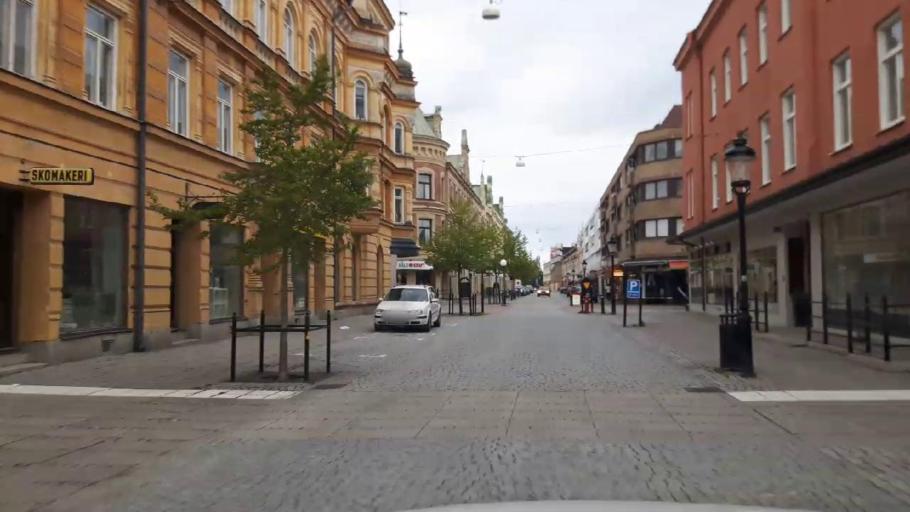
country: SE
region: Vaestmanland
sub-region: Kopings Kommun
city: Koping
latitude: 59.5122
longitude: 15.9954
